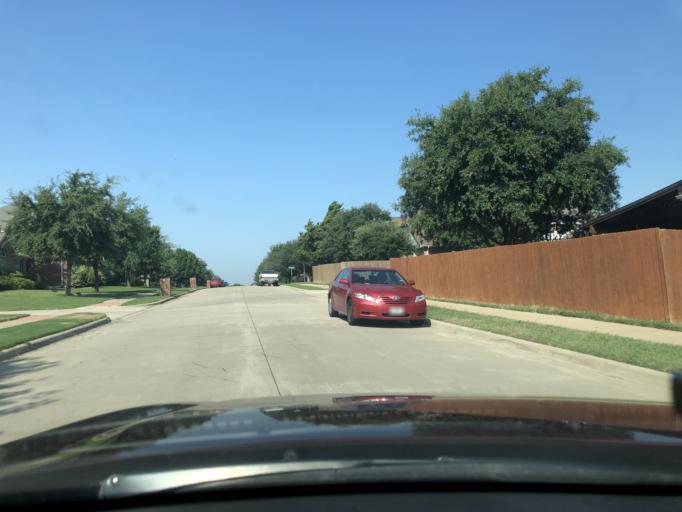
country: US
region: Texas
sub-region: Rockwall County
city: Rockwall
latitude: 32.9417
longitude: -96.4673
